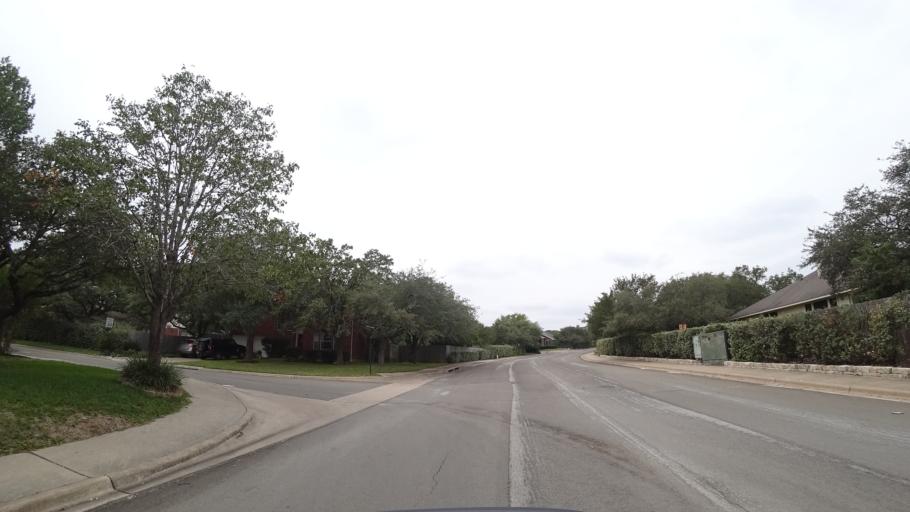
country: US
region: Texas
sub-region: Travis County
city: Shady Hollow
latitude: 30.2125
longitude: -97.8861
